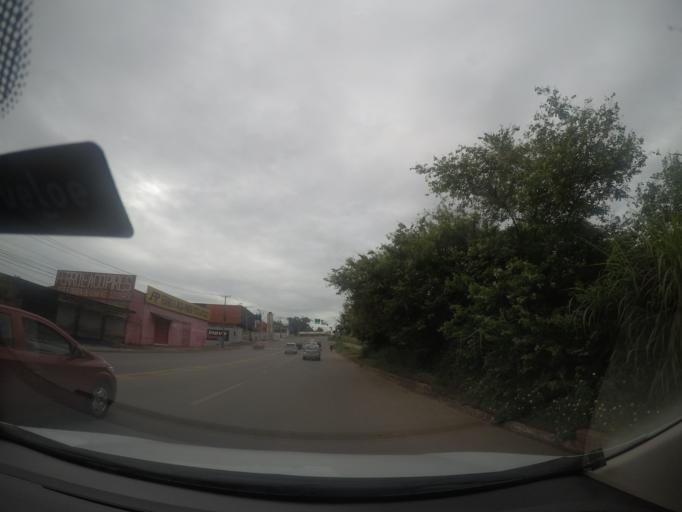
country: BR
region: Goias
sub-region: Goiania
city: Goiania
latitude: -16.6333
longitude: -49.2839
